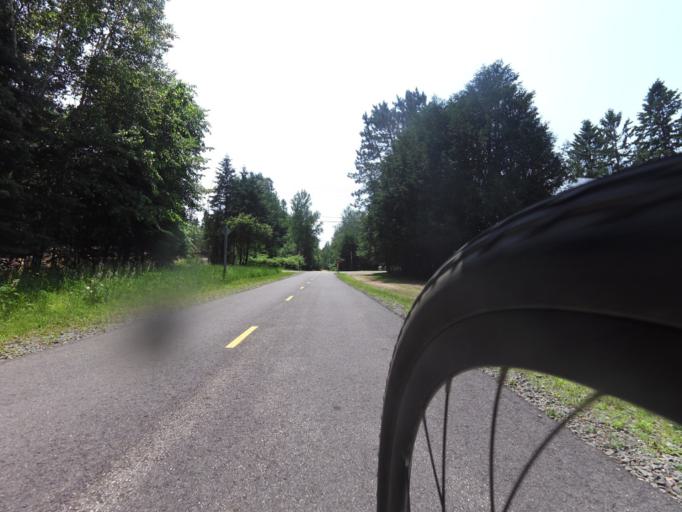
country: CA
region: Quebec
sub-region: Laurentides
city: Mont-Tremblant
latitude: 46.1381
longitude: -74.5965
